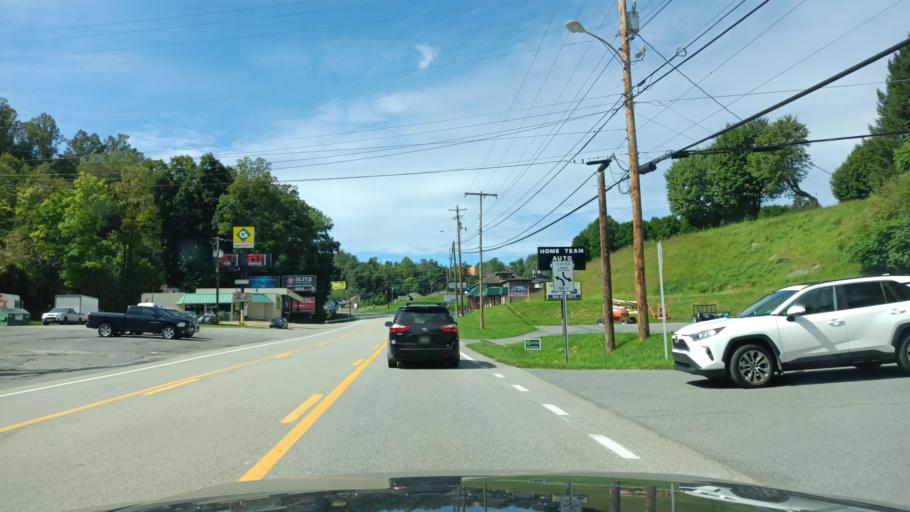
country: US
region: West Virginia
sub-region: Harrison County
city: Bridgeport
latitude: 39.2817
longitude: -80.2649
